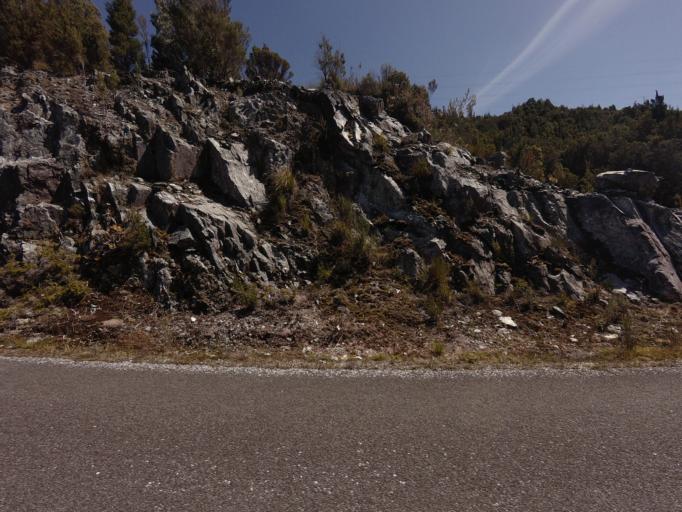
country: AU
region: Tasmania
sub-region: West Coast
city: Queenstown
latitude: -42.7433
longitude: 145.9808
